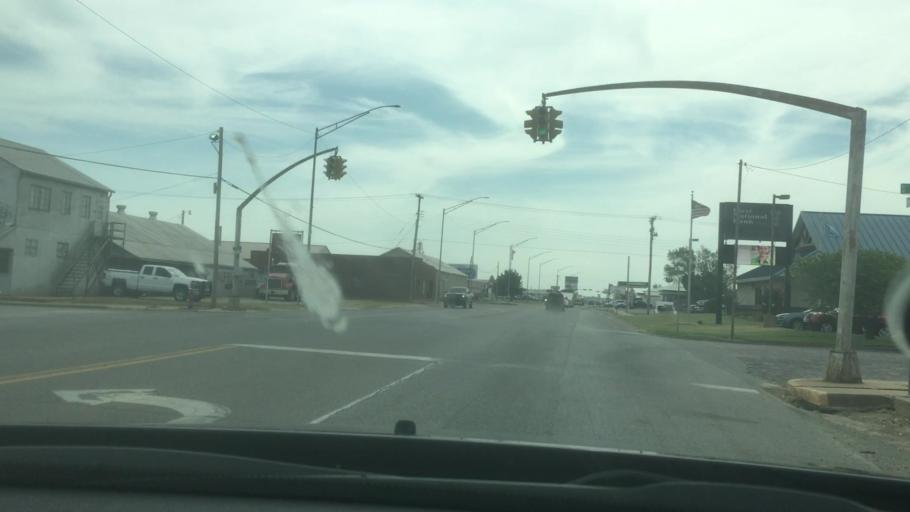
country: US
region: Oklahoma
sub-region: Garvin County
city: Lindsay
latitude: 34.8368
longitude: -97.6031
